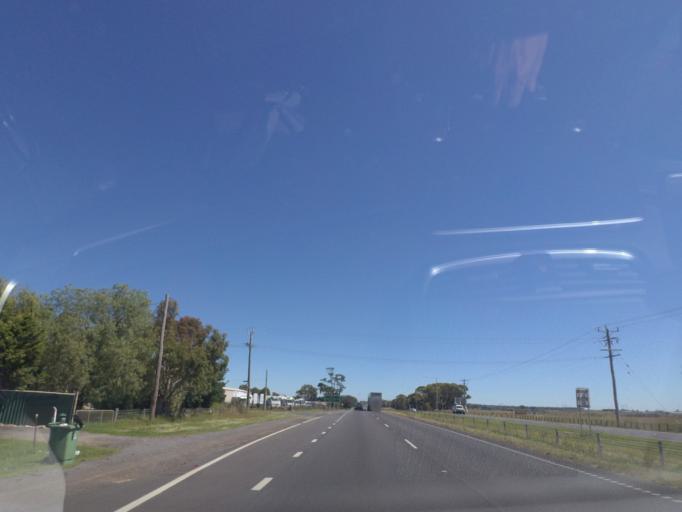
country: AU
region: Victoria
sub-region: Hume
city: Craigieburn
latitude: -37.5300
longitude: 144.9473
